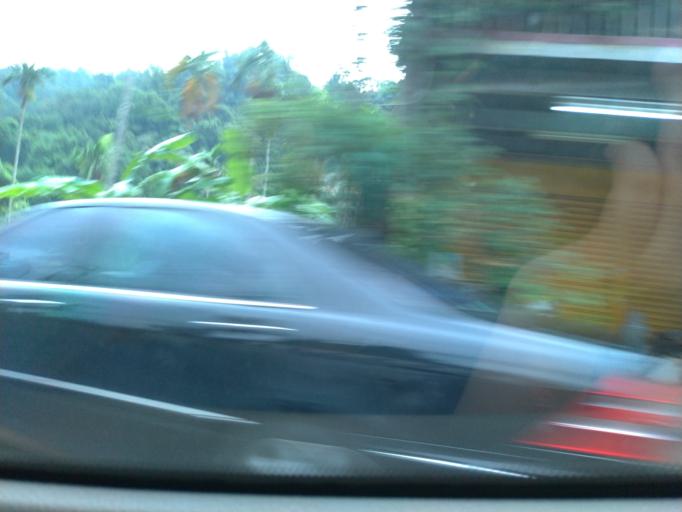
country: TW
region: Taipei
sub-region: Taipei
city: Banqiao
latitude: 24.9251
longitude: 121.4266
